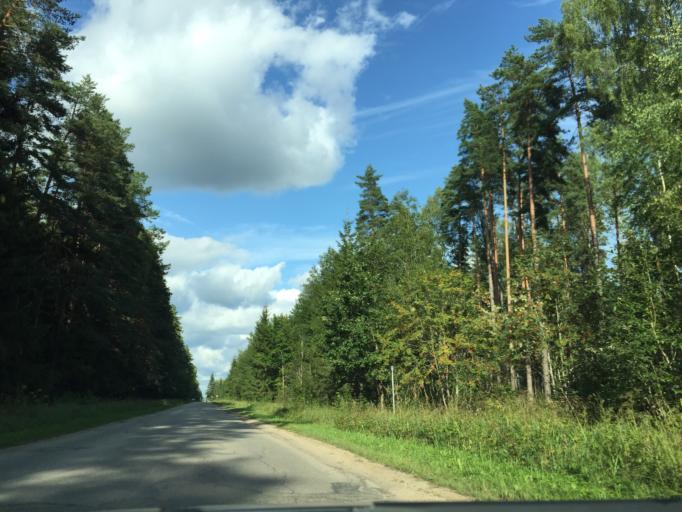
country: LV
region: Ogre
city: Ogre
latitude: 56.8264
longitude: 24.6394
